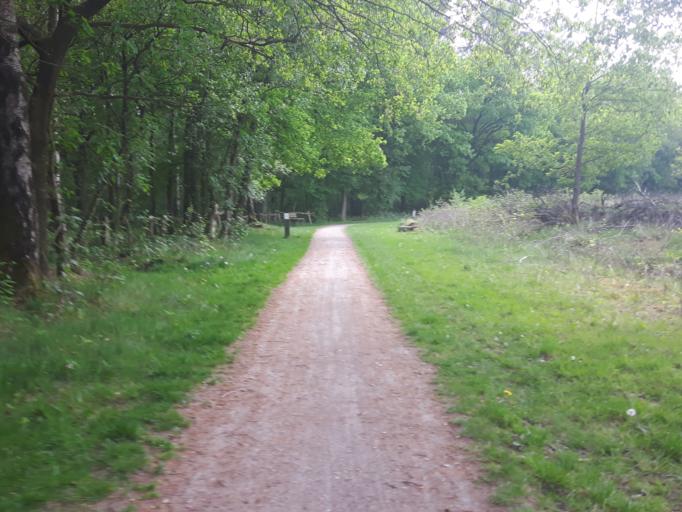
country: NL
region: Overijssel
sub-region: Gemeente Enschede
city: Enschede
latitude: 52.1465
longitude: 6.8698
